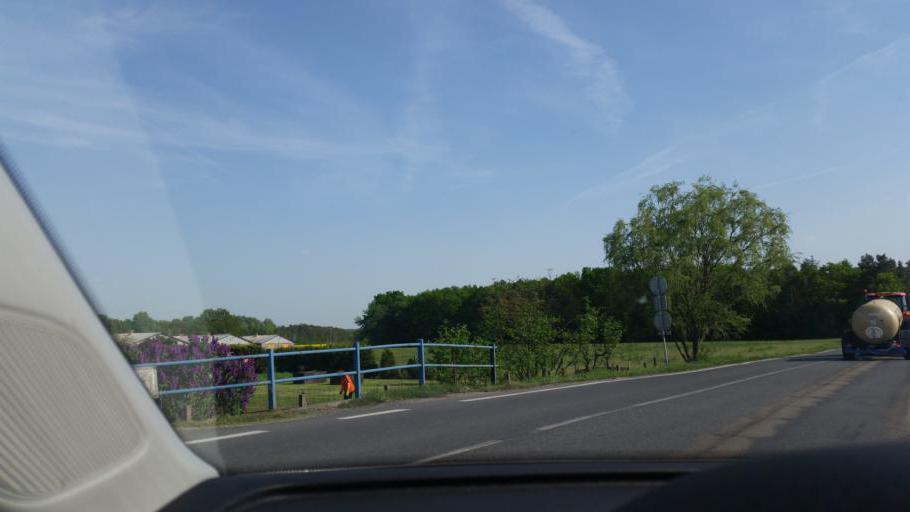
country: CZ
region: Central Bohemia
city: Veltruby
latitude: 50.0596
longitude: 15.1965
